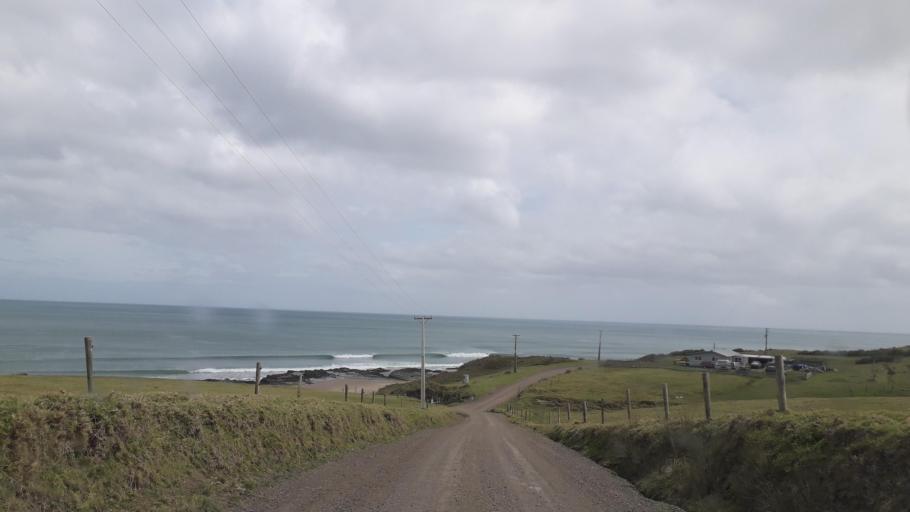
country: NZ
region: Northland
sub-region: Far North District
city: Ahipara
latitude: -35.4300
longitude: 173.2739
